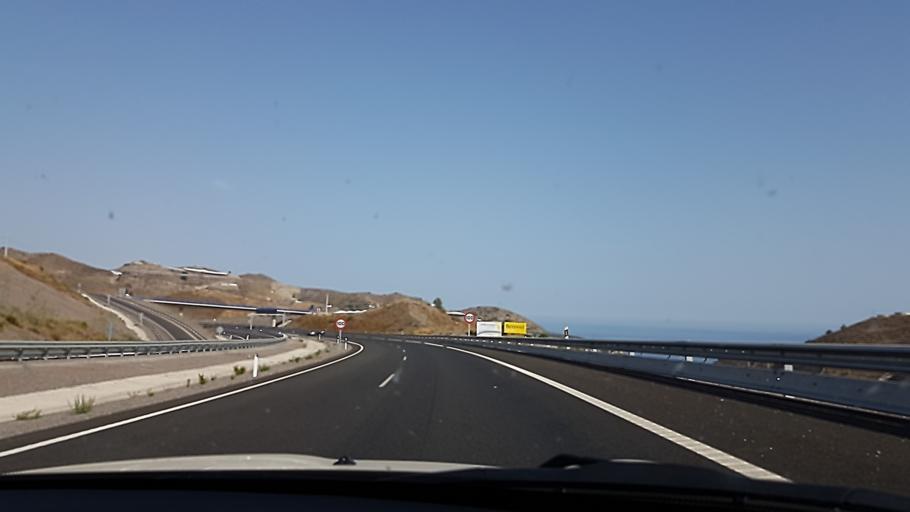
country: ES
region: Andalusia
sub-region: Provincia de Granada
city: Polopos
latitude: 36.7492
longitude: -3.3161
